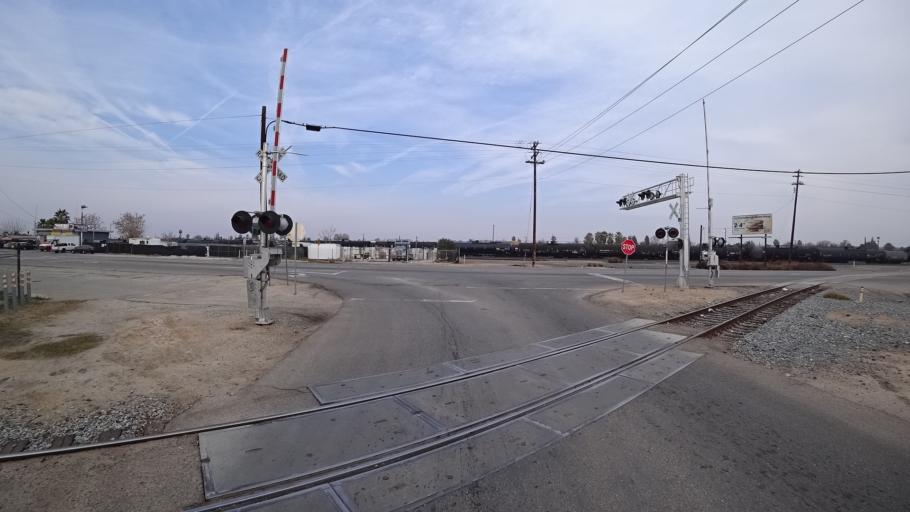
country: US
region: California
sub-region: Kern County
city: Bakersfield
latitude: 35.3726
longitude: -118.9764
